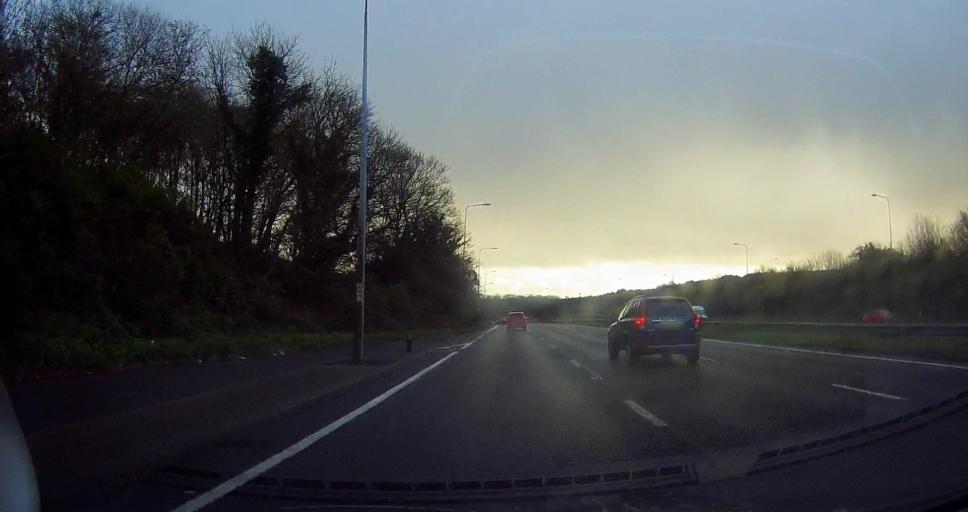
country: GB
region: England
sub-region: Brighton and Hove
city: Hove
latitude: 50.8783
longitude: -0.1644
